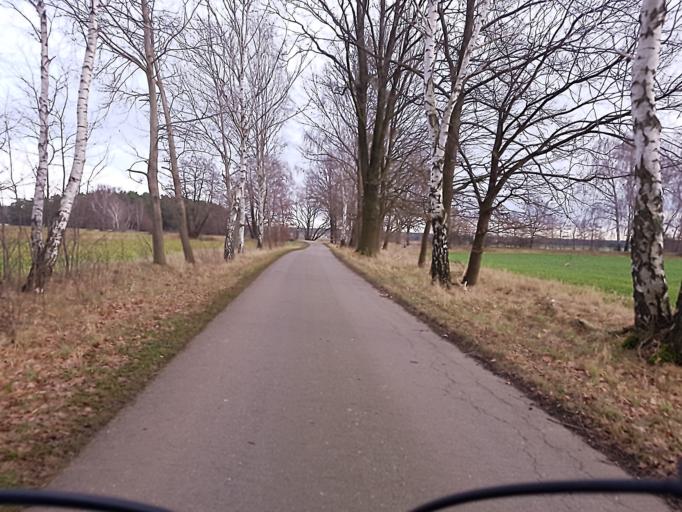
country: DE
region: Brandenburg
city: Schilda
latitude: 51.5708
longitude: 13.3908
